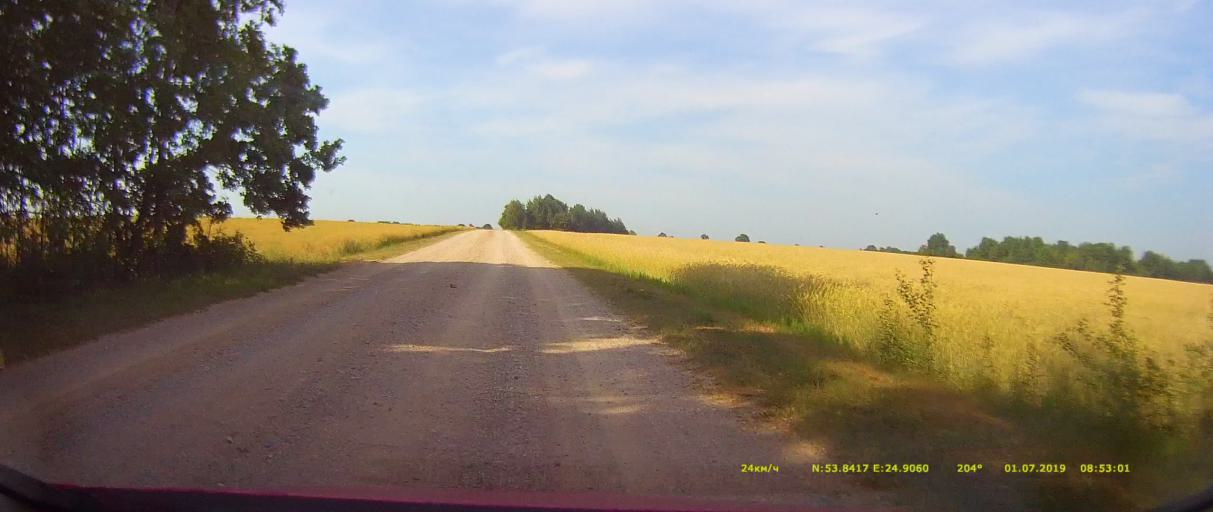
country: BY
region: Grodnenskaya
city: Shchuchin
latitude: 53.8417
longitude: 24.9063
